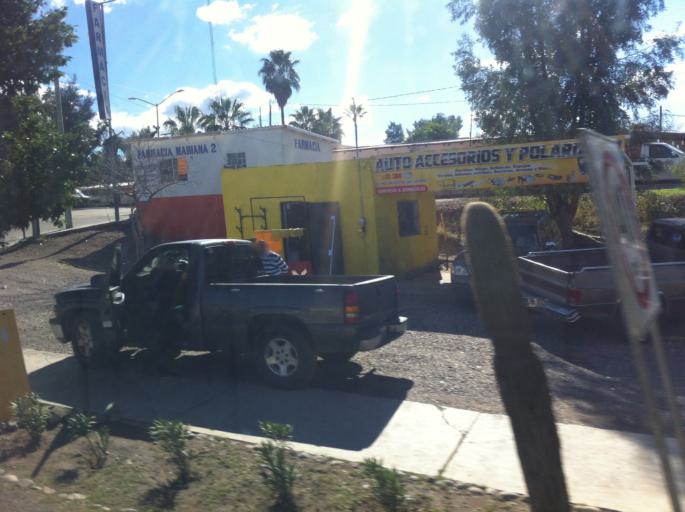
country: MX
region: Sonora
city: Santa Ana
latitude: 30.5434
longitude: -111.1137
